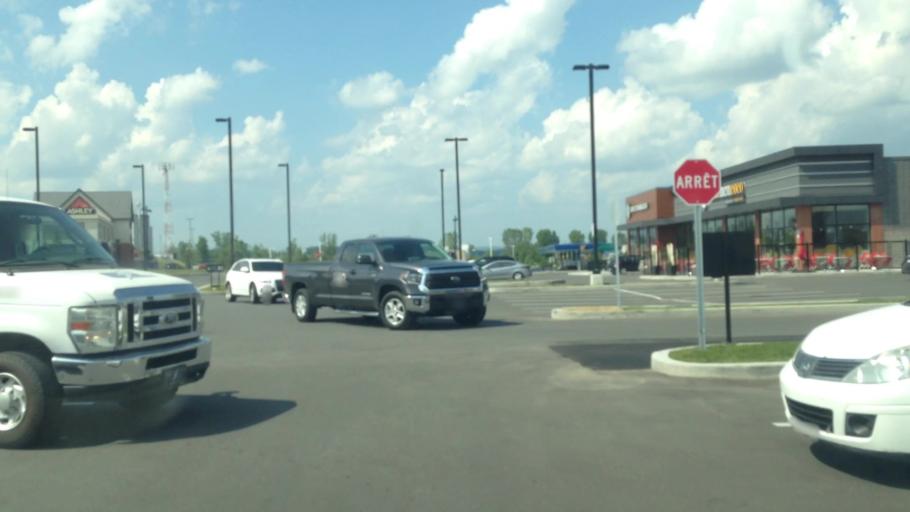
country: CA
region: Quebec
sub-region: Laurentides
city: Saint-Jerome
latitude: 45.7595
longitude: -74.0234
